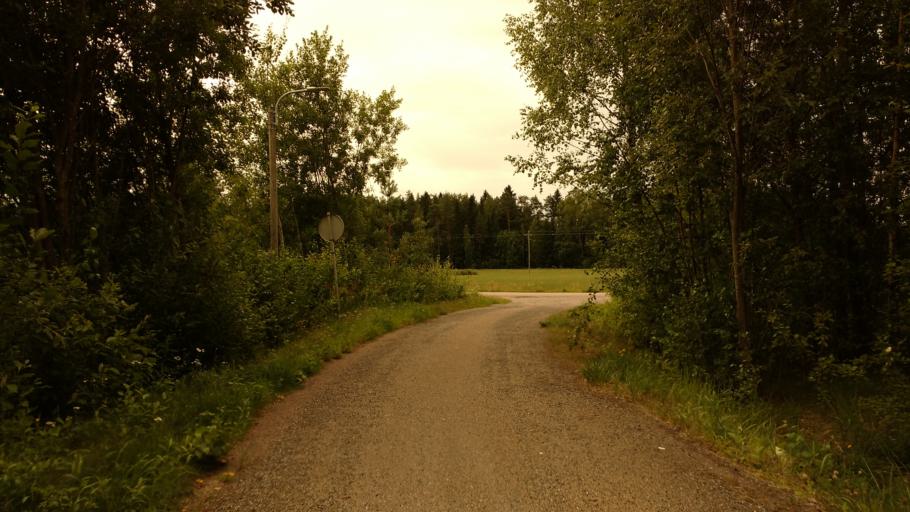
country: FI
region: Varsinais-Suomi
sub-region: Turku
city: Kaarina
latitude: 60.4429
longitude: 22.4328
